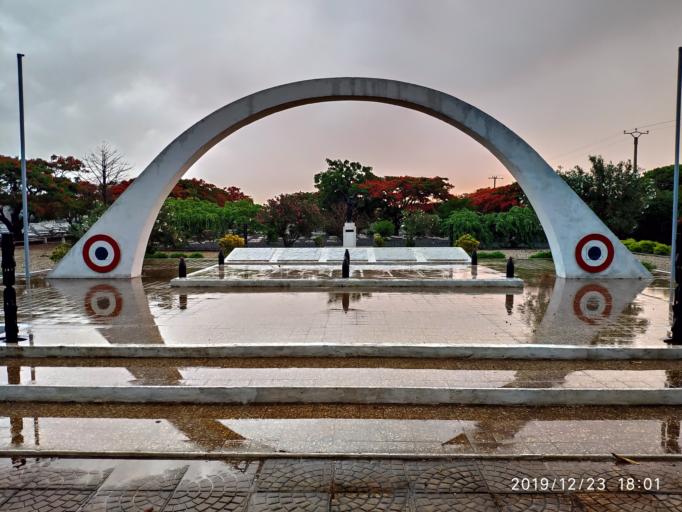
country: MG
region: Diana
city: Antsiranana
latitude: -12.2880
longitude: 49.2956
